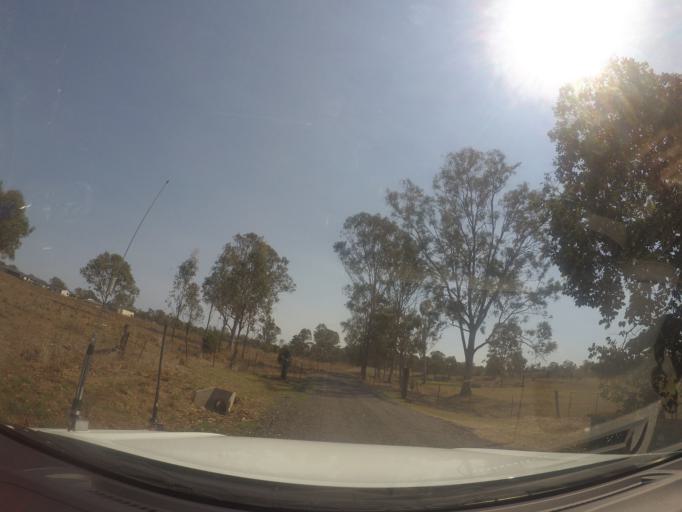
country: AU
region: Queensland
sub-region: Logan
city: North Maclean
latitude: -27.7861
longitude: 153.0280
